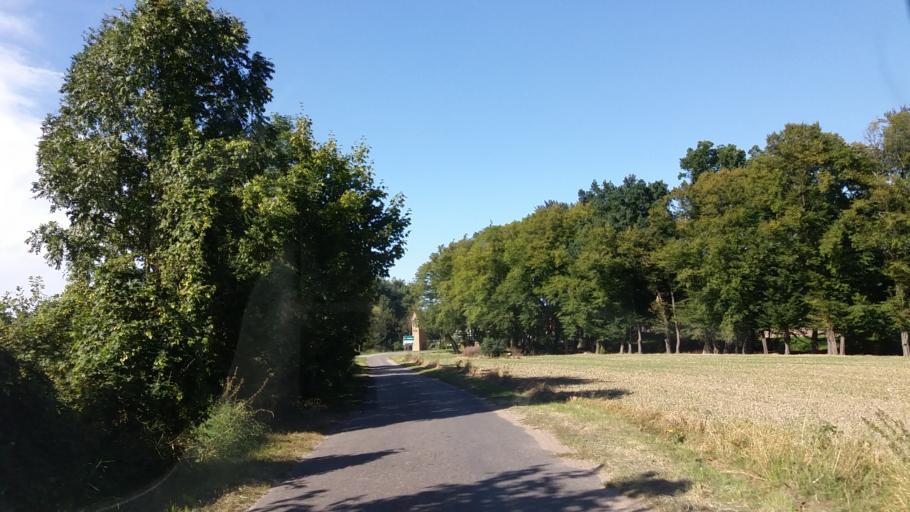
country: PL
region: West Pomeranian Voivodeship
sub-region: Powiat choszczenski
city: Krzecin
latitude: 53.1117
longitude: 15.4935
